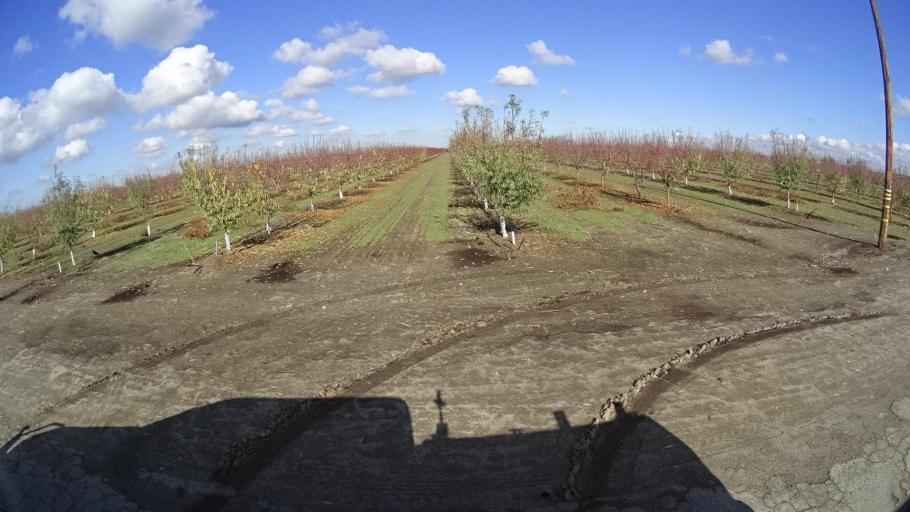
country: US
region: California
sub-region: Kern County
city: Wasco
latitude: 35.6670
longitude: -119.3278
